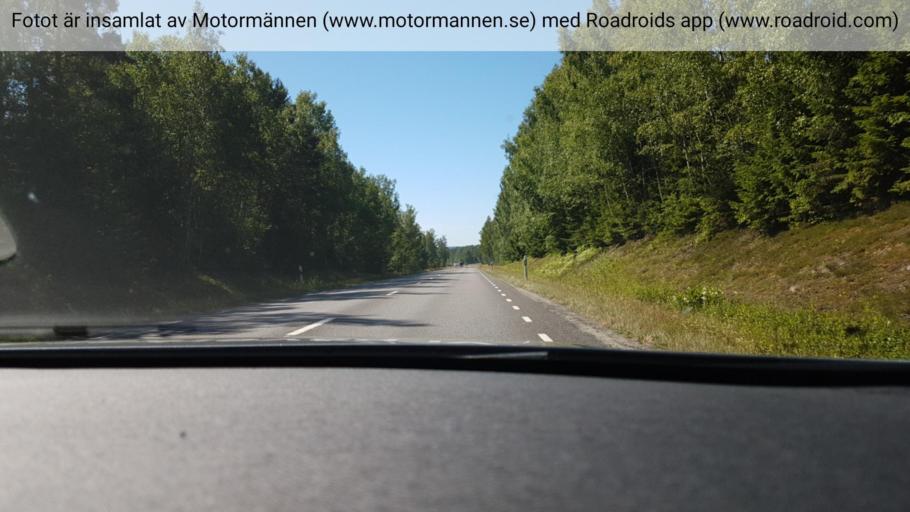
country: SE
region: Joenkoeping
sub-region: Habo Kommun
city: Habo
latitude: 57.9741
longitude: 14.1052
